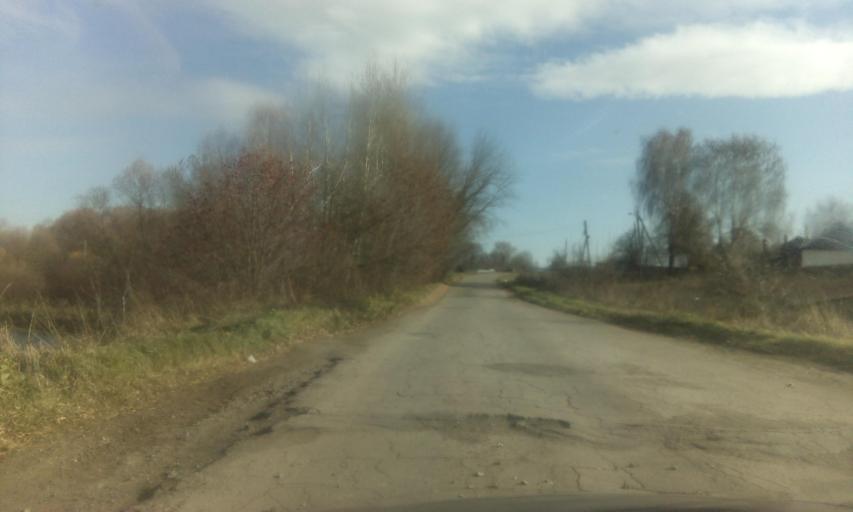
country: RU
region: Tula
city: Dubovka
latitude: 53.9464
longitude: 38.0321
